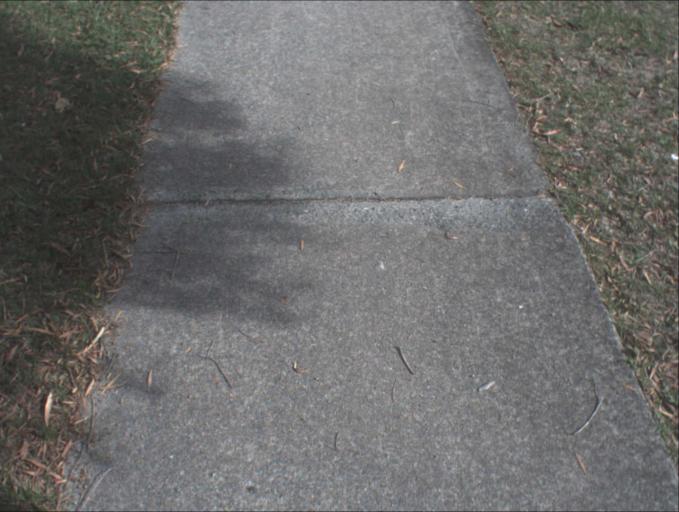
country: AU
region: Queensland
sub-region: Logan
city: Logan Reserve
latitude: -27.6874
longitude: 153.0879
